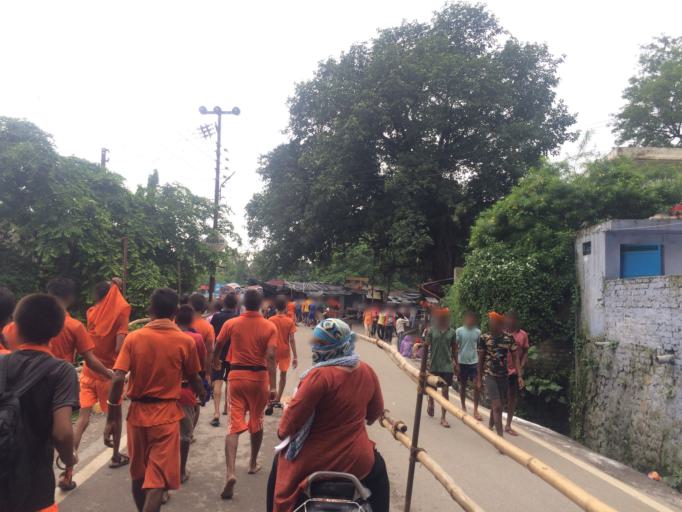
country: IN
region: Uttarakhand
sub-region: Dehradun
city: Rishikesh
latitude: 30.1213
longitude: 78.3085
